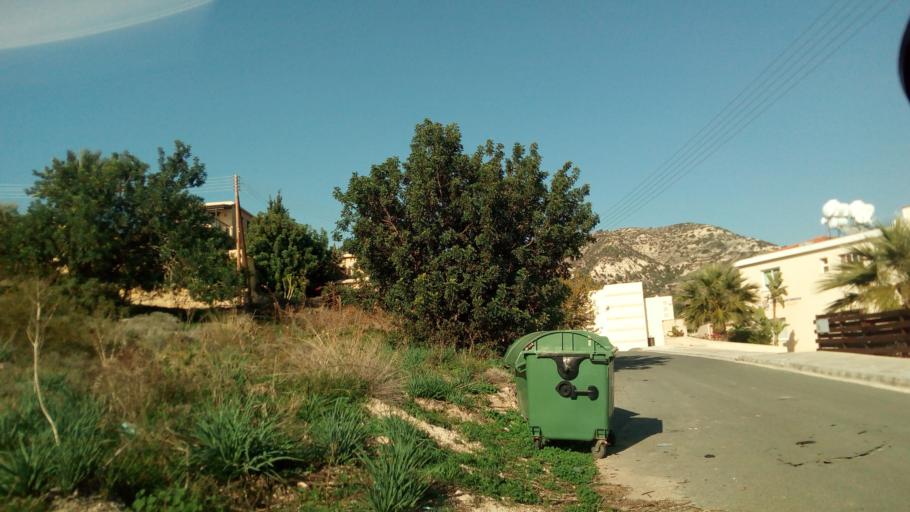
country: CY
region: Pafos
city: Pegeia
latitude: 34.8826
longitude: 32.3900
